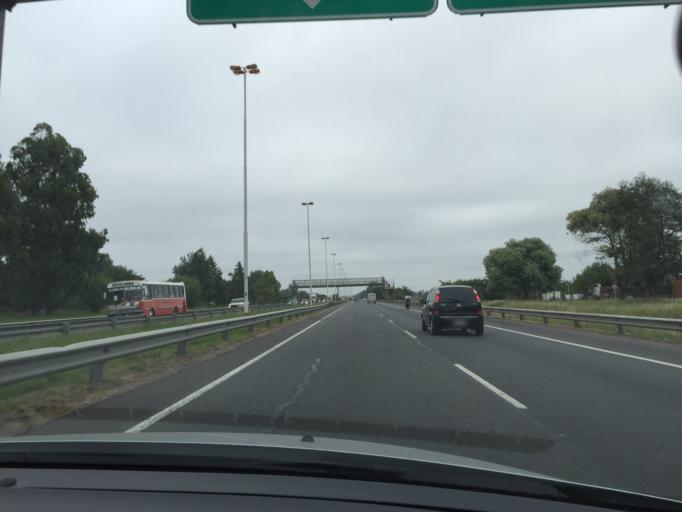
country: AR
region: Buenos Aires
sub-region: Partido de Ezeiza
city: Ezeiza
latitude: -34.8410
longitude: -58.5269
